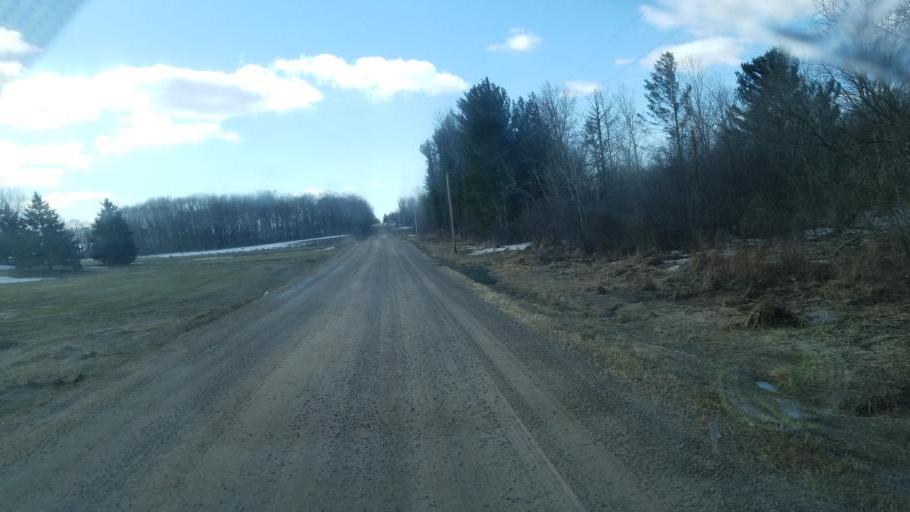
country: US
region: Wisconsin
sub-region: Clark County
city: Loyal
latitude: 44.6785
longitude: -90.4558
